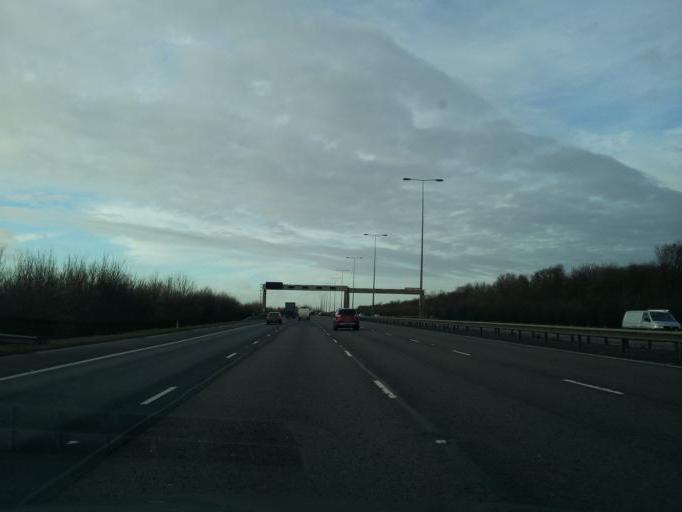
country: GB
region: England
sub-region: Cambridgeshire
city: Stilton
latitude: 52.4716
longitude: -0.2846
